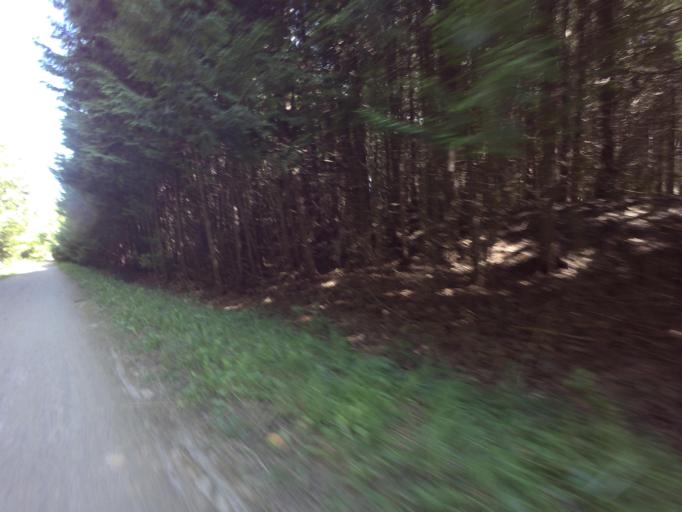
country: CA
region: Ontario
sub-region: Wellington County
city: Guelph
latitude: 43.7803
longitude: -80.3248
